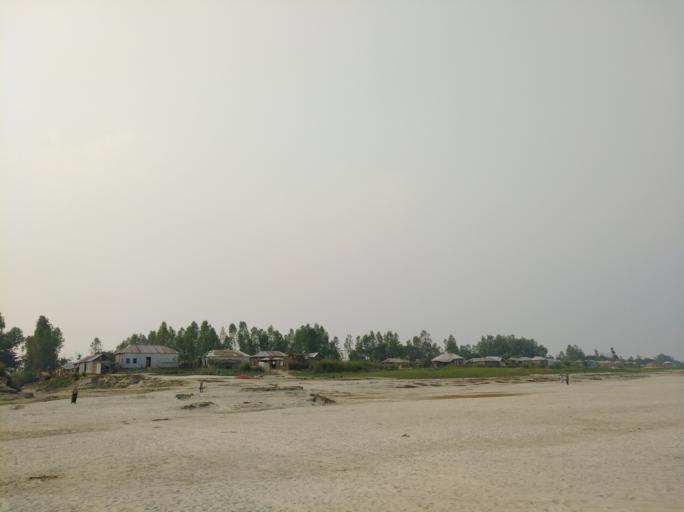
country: BD
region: Dhaka
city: Nagarpur
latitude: 24.0033
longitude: 89.7848
